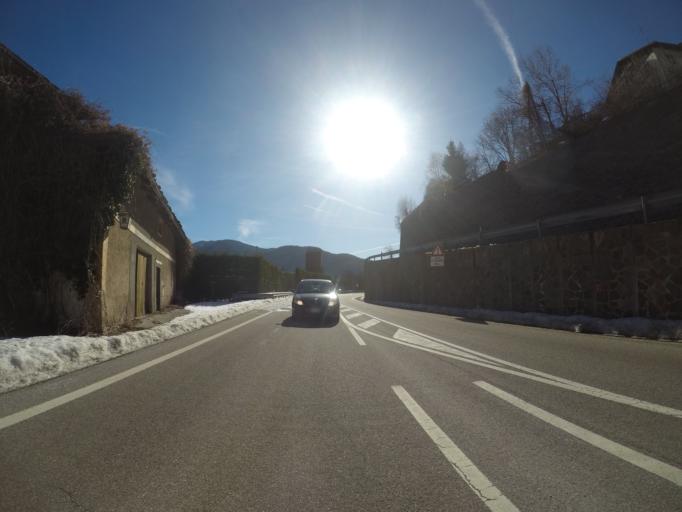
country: IT
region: Trentino-Alto Adige
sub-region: Provincia di Trento
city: Capriana
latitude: 46.2620
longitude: 11.3441
